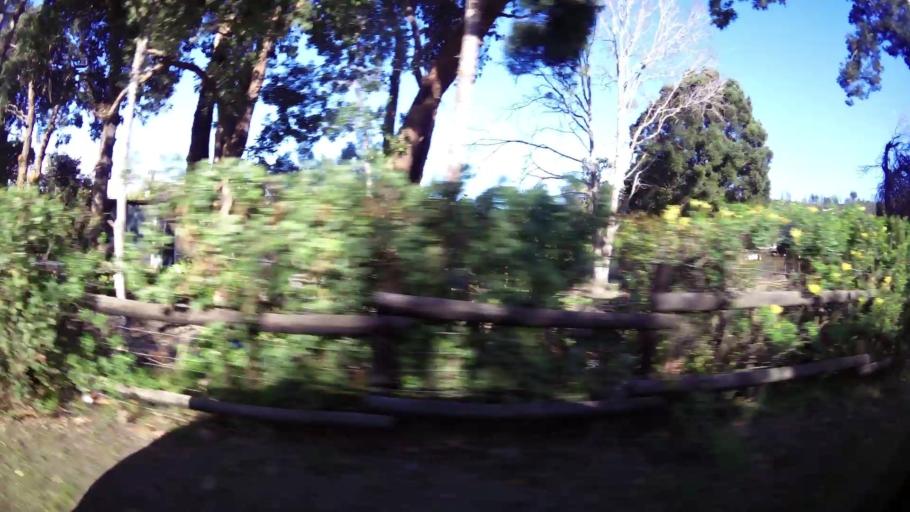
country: ZA
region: Western Cape
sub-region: Eden District Municipality
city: Knysna
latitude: -34.0358
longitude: 23.0164
